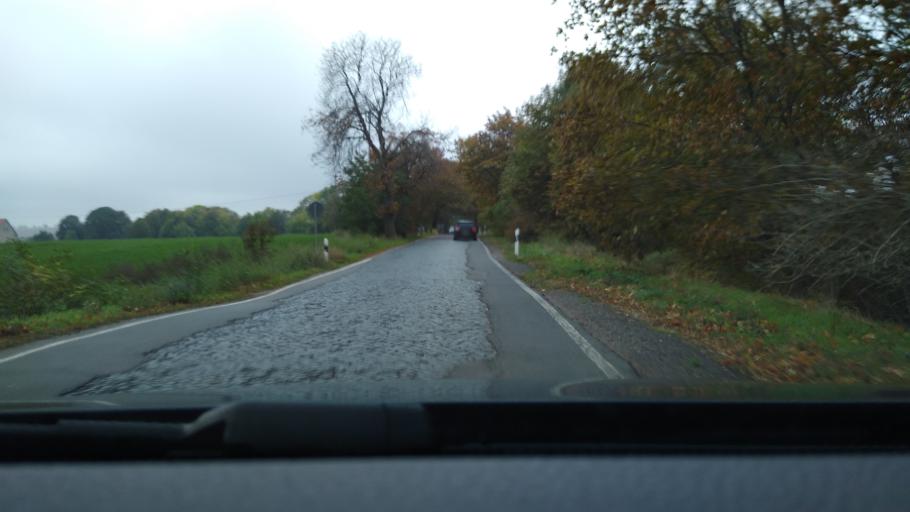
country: DE
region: Saxony-Anhalt
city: Gerbstedt
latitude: 51.6111
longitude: 11.6143
